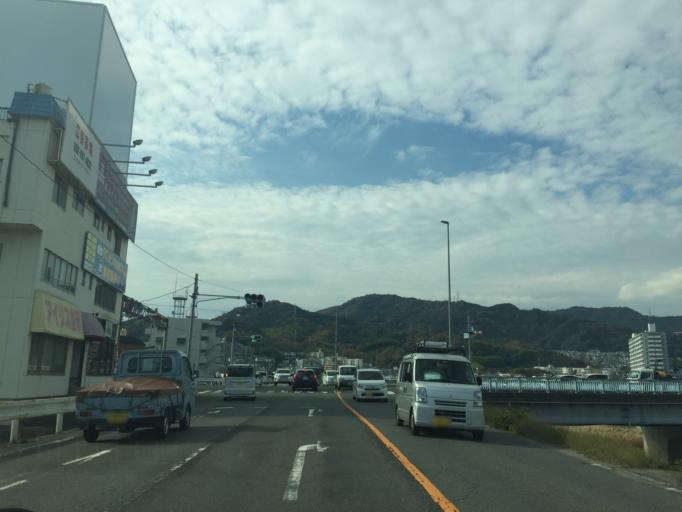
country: JP
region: Hiroshima
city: Hiroshima-shi
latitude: 34.4242
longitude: 132.4605
